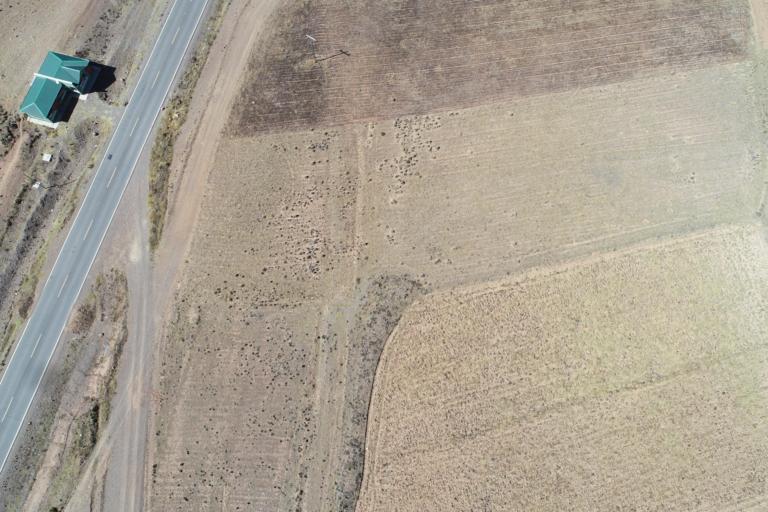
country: BO
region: La Paz
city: Achacachi
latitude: -15.9032
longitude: -68.8988
